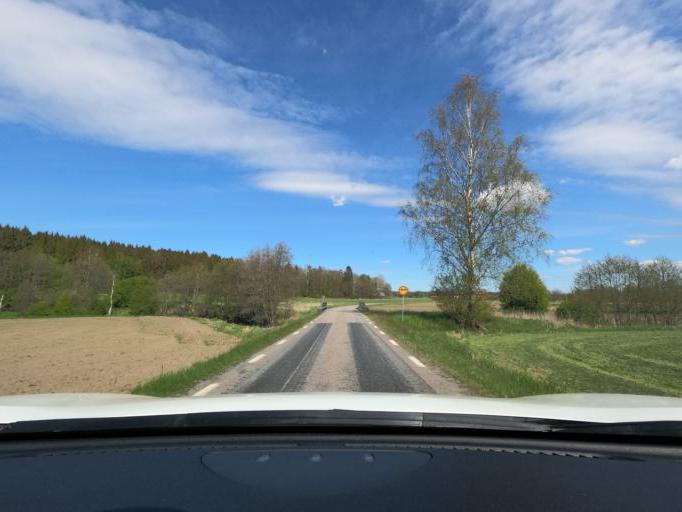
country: SE
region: Vaestra Goetaland
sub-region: Marks Kommun
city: Horred
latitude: 57.4504
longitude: 12.4681
